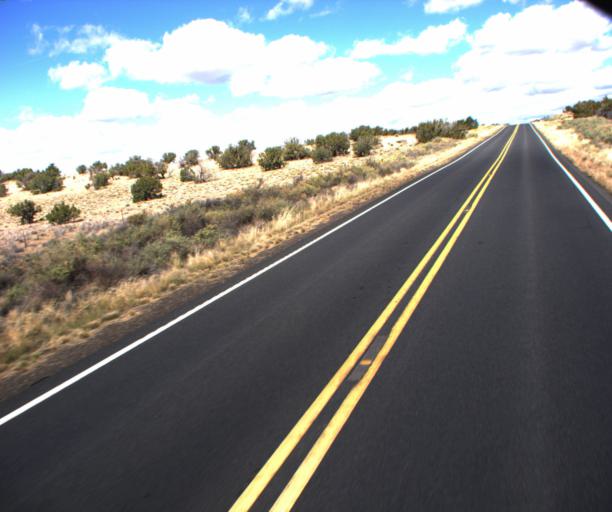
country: US
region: Arizona
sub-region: Apache County
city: Houck
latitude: 35.1004
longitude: -109.3138
